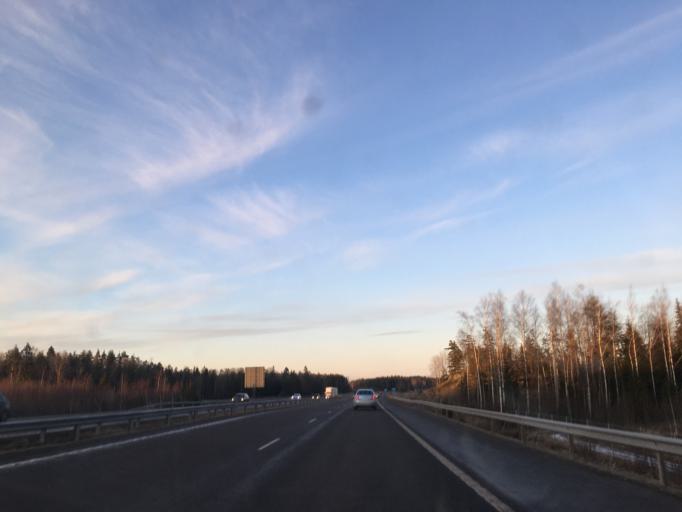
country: FI
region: Varsinais-Suomi
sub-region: Turku
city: Turku
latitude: 60.5167
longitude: 22.3030
